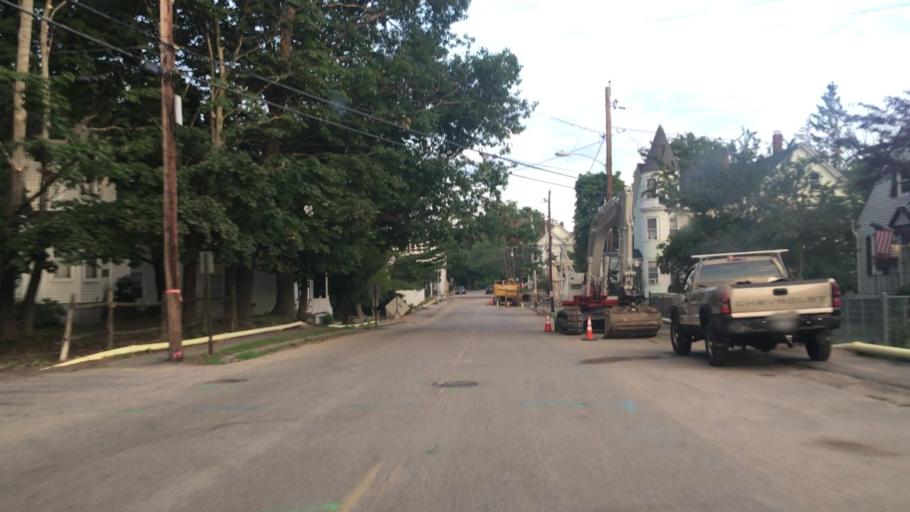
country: US
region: Maine
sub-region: Cumberland County
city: South Portland
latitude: 43.6325
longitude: -70.2680
